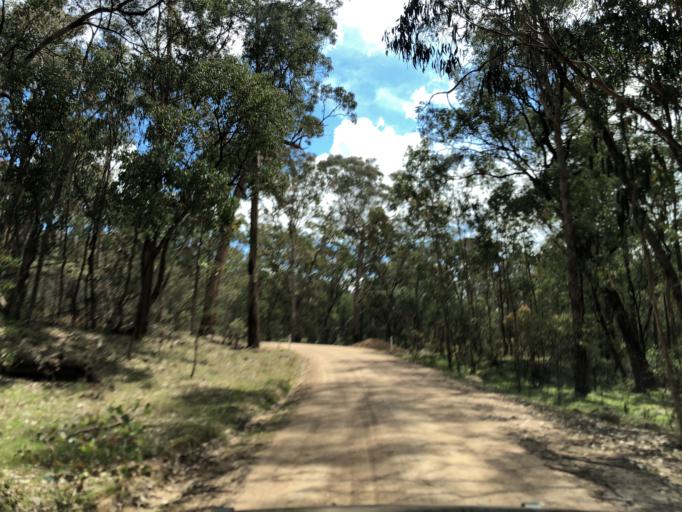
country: AU
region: Victoria
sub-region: Benalla
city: Benalla
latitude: -36.7460
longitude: 146.1592
